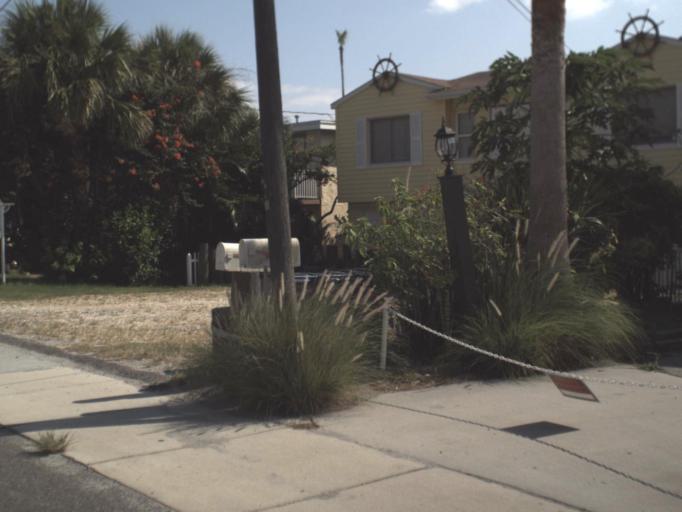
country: US
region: Florida
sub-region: Pinellas County
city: Treasure Island
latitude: 27.7594
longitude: -82.7656
